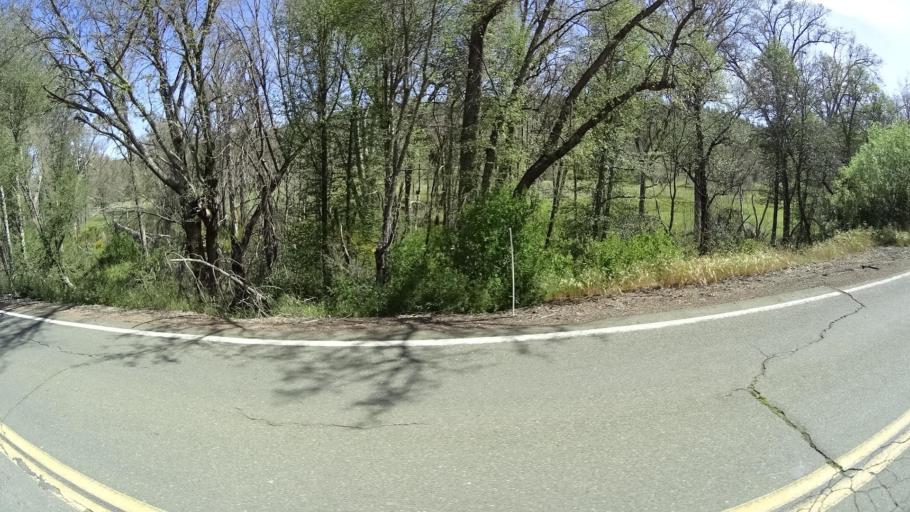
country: US
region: California
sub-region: Lake County
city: Cobb
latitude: 38.8410
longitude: -122.7478
